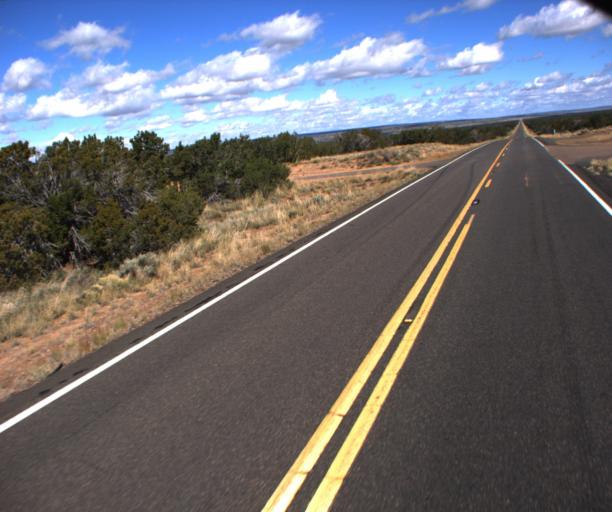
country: US
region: Arizona
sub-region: Apache County
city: Saint Johns
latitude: 34.8491
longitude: -109.2376
